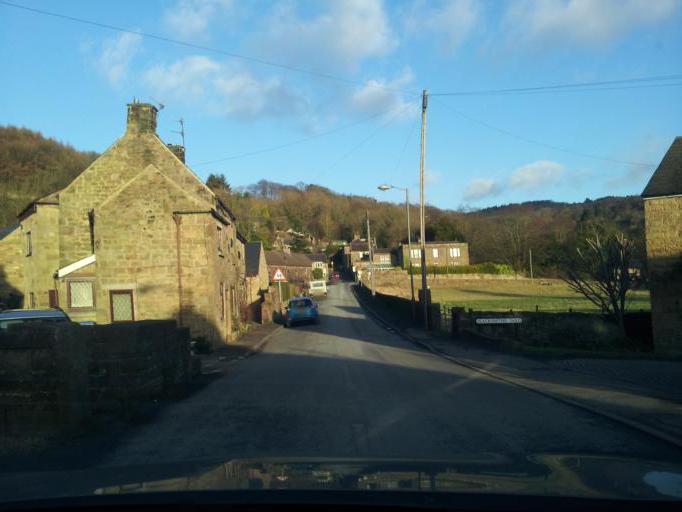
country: GB
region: England
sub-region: Derbyshire
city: Matlock
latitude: 53.1631
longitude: -1.5821
